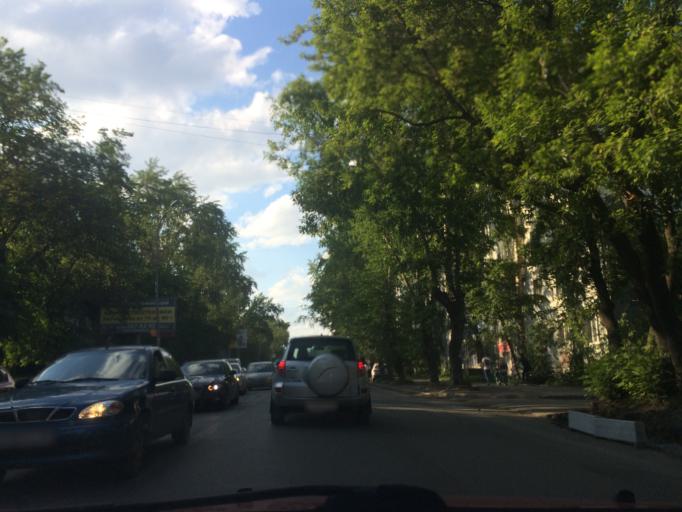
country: RU
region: Sverdlovsk
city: Yekaterinburg
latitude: 56.8240
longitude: 60.6388
